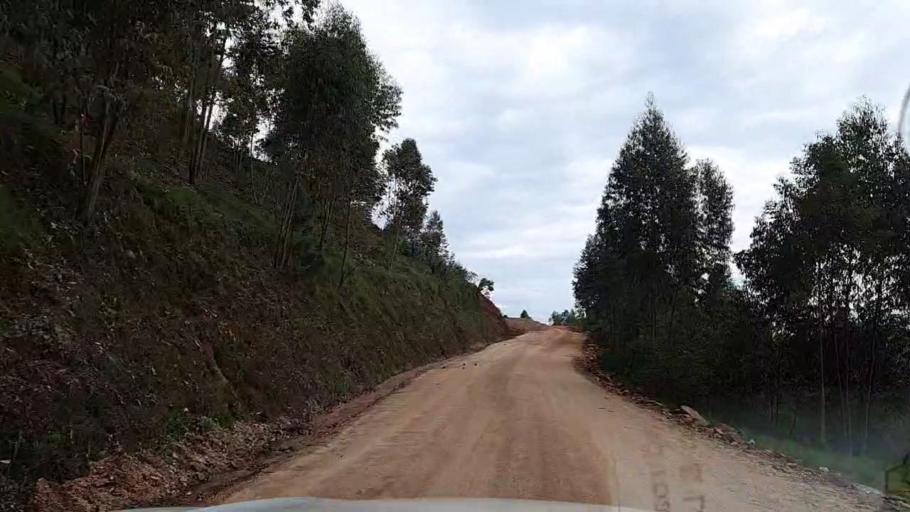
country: RW
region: Southern Province
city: Nzega
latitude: -2.3698
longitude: 29.4503
